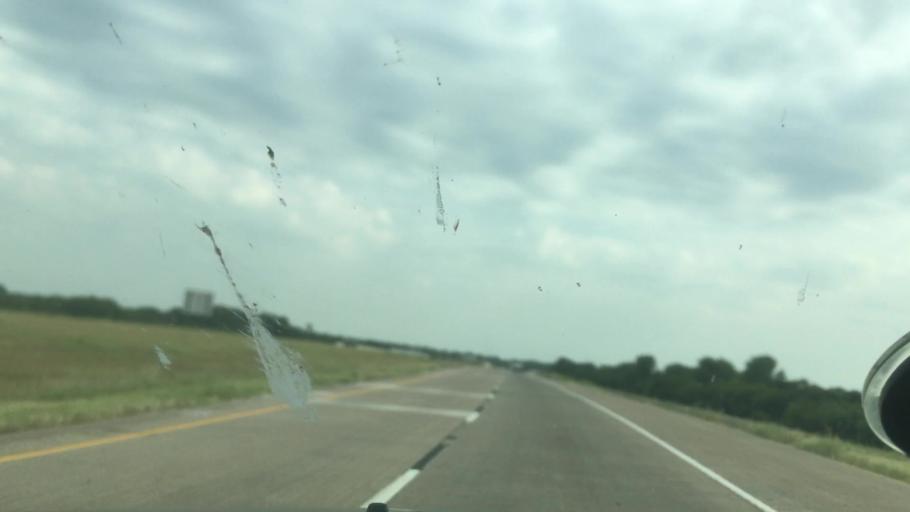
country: US
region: Texas
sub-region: Grayson County
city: Denison
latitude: 33.8077
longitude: -96.5346
